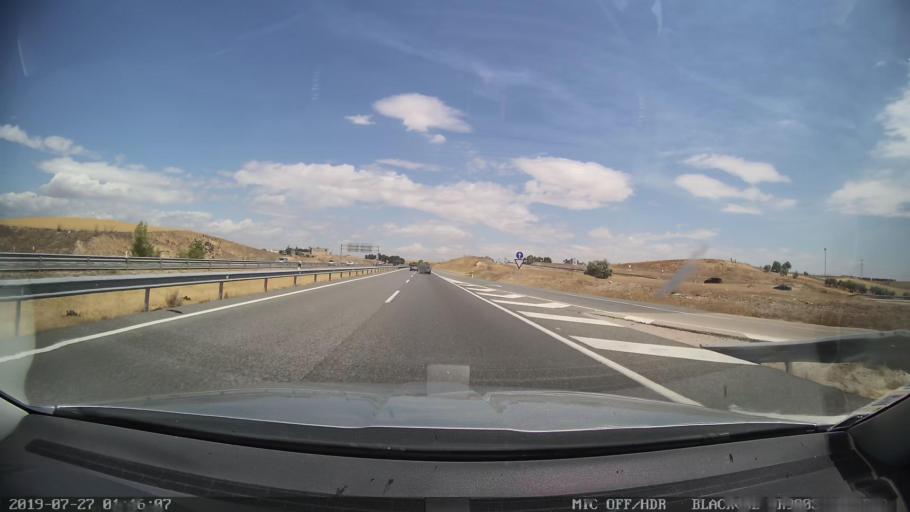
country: ES
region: Castille-La Mancha
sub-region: Province of Toledo
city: Maqueda
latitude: 40.0564
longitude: -4.3756
